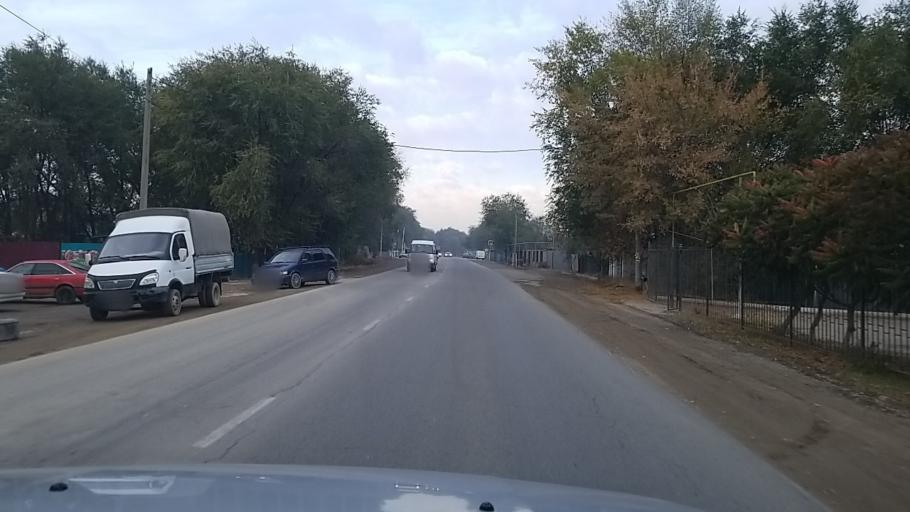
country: KZ
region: Almaty Oblysy
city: Burunday
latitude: 43.3536
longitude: 76.8210
